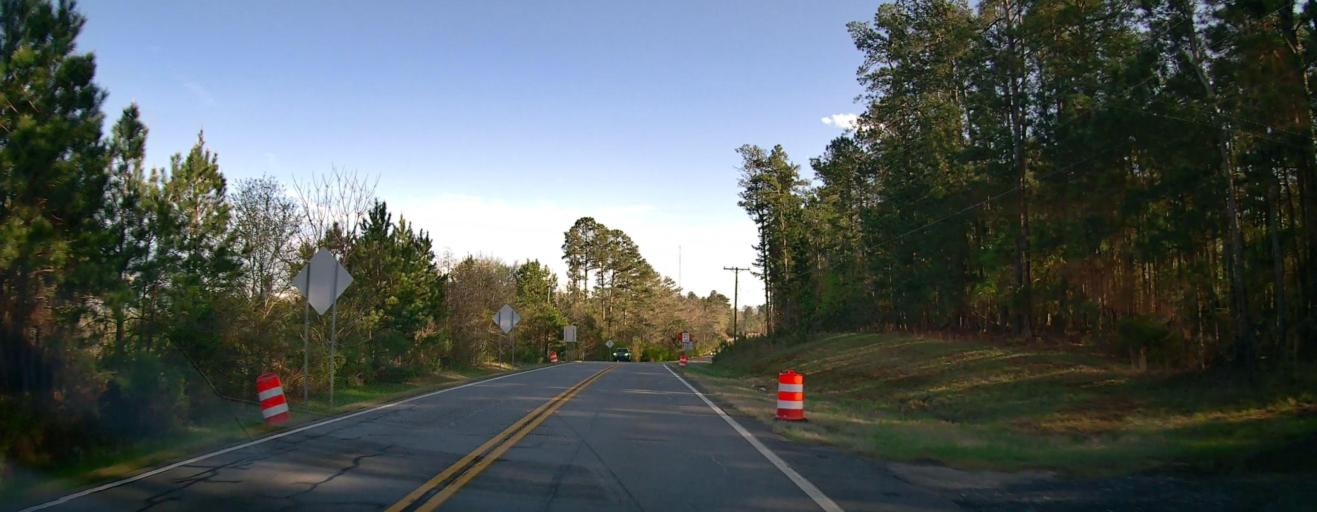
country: US
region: Georgia
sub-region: Baldwin County
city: Milledgeville
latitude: 33.1151
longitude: -83.2866
